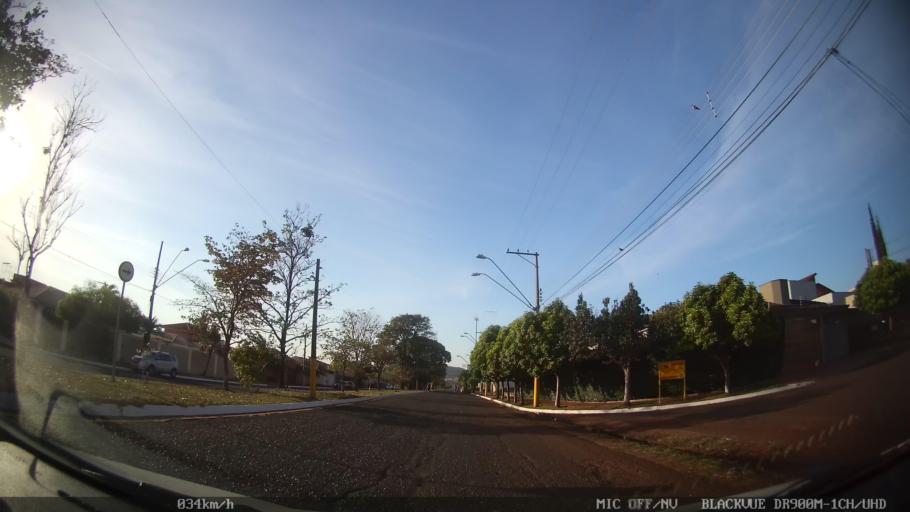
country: BR
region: Sao Paulo
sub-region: Ribeirao Preto
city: Ribeirao Preto
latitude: -21.2179
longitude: -47.7783
